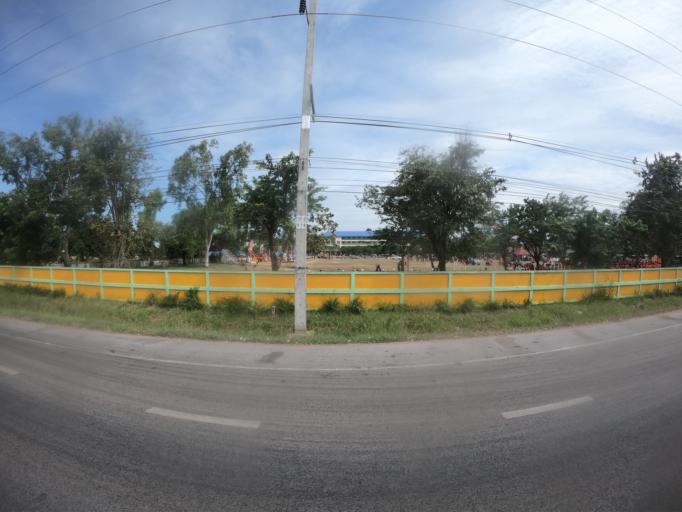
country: TH
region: Maha Sarakham
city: Chiang Yuen
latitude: 16.4293
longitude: 103.0624
